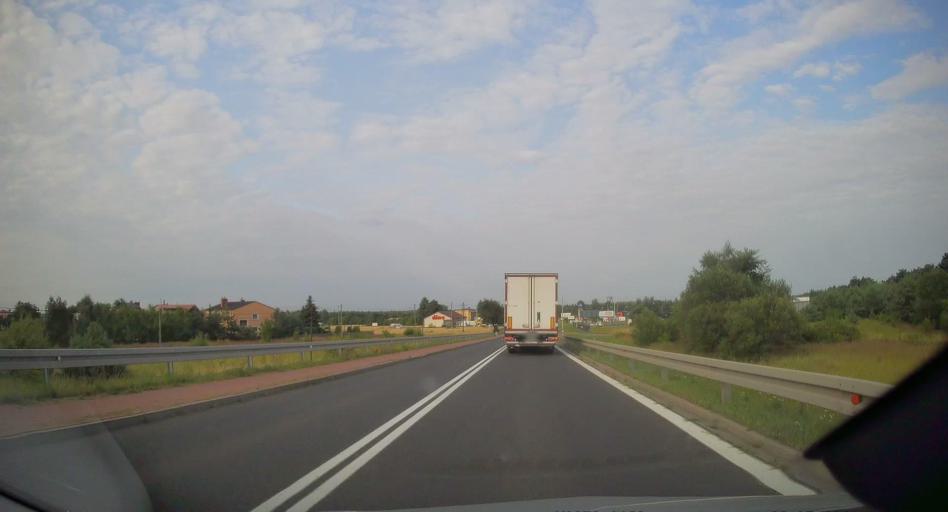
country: PL
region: Silesian Voivodeship
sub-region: Powiat czestochowski
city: Rudniki
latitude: 50.8823
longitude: 19.2532
